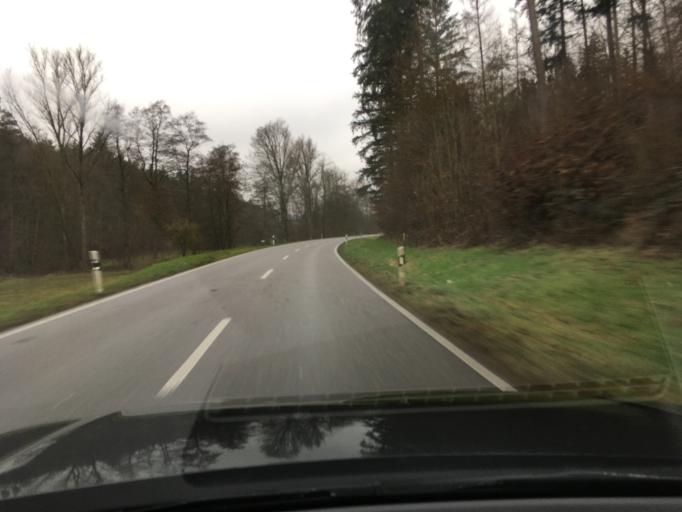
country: DE
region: Baden-Wuerttemberg
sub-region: Karlsruhe Region
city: Konigsbach-Stein
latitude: 48.9511
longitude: 8.5360
